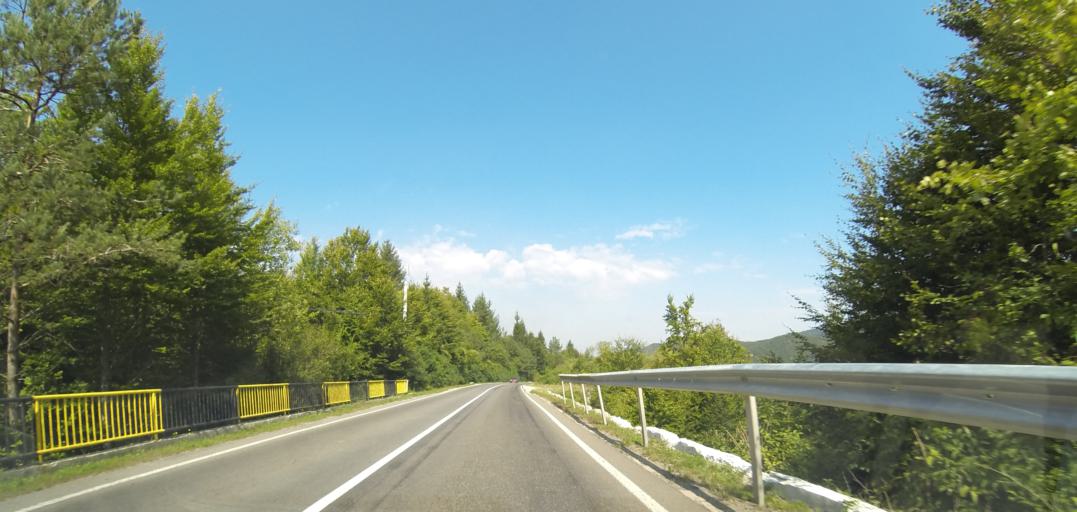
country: RO
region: Brasov
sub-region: Comuna Tarlungeni
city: Tarlungeni
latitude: 45.5819
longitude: 25.7587
